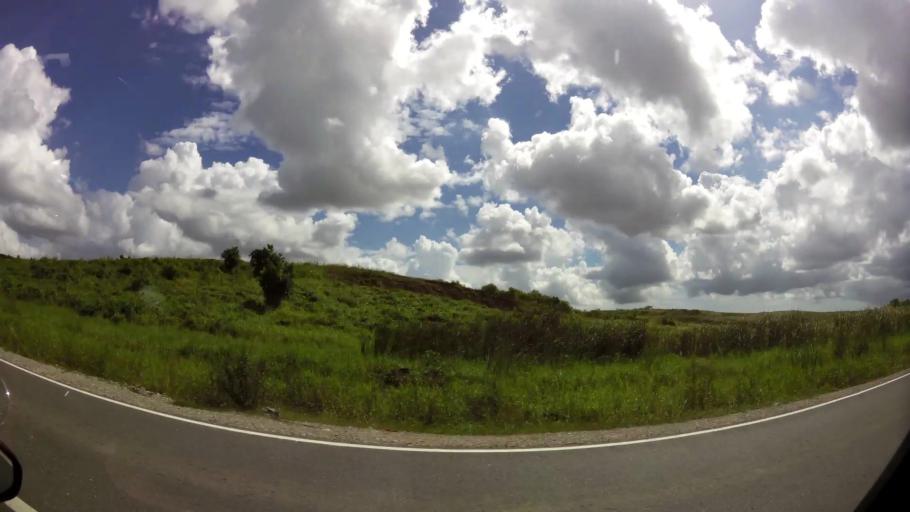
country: TT
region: Penal/Debe
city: Debe
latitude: 10.2298
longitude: -61.4904
